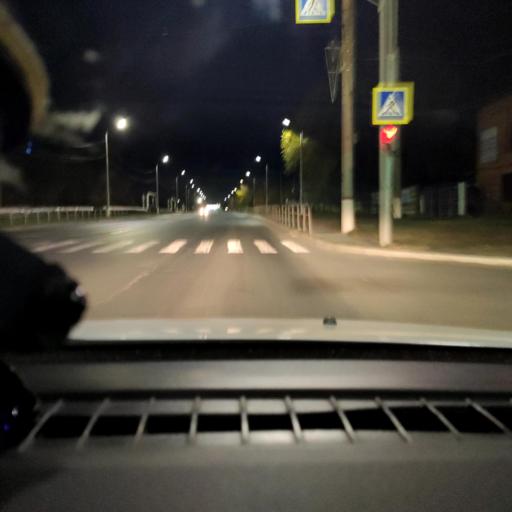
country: RU
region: Samara
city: Novokuybyshevsk
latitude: 53.0945
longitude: 49.9404
